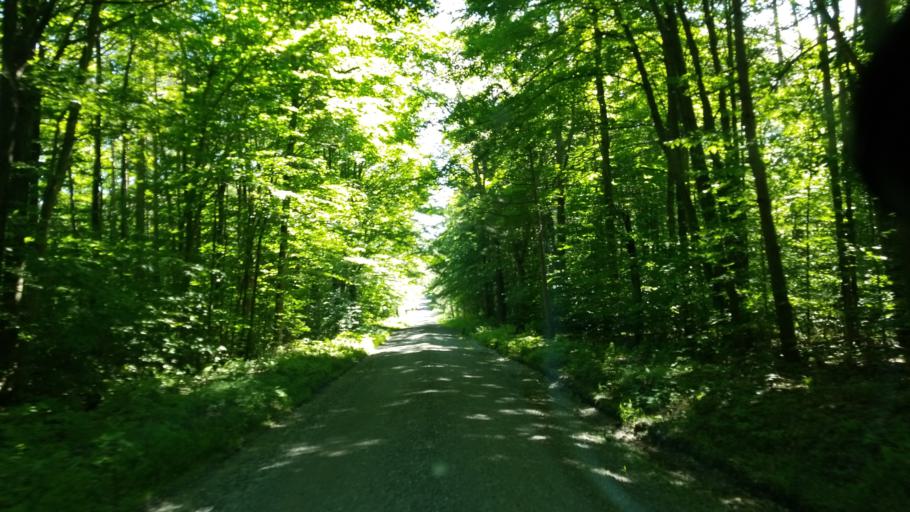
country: US
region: Pennsylvania
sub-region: Clearfield County
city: Clearfield
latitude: 41.2084
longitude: -78.4157
